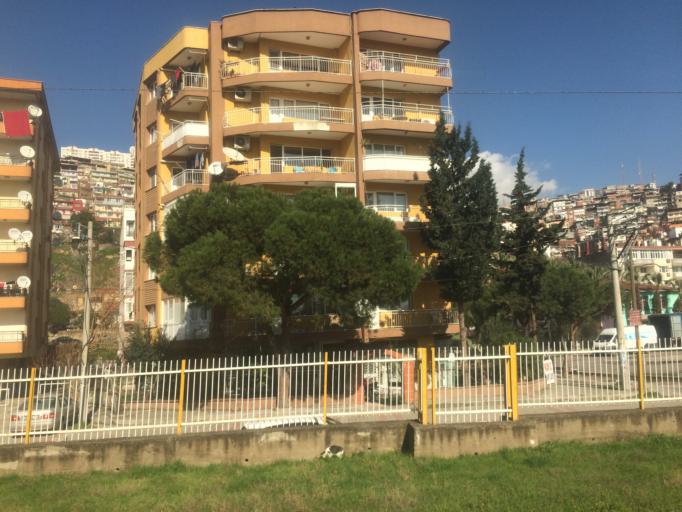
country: TR
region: Izmir
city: Karsiyaka
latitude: 38.4684
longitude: 27.1578
